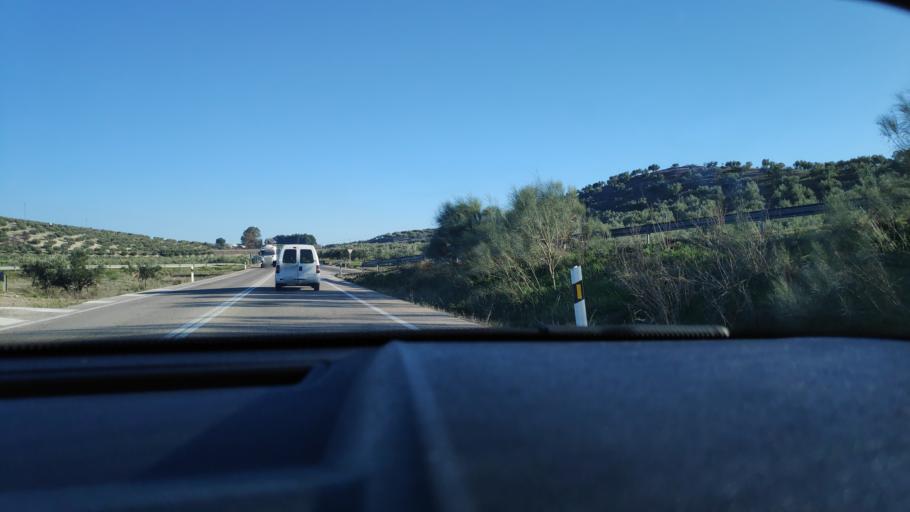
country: ES
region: Andalusia
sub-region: Province of Cordoba
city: Luque
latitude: 37.5764
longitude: -4.2719
